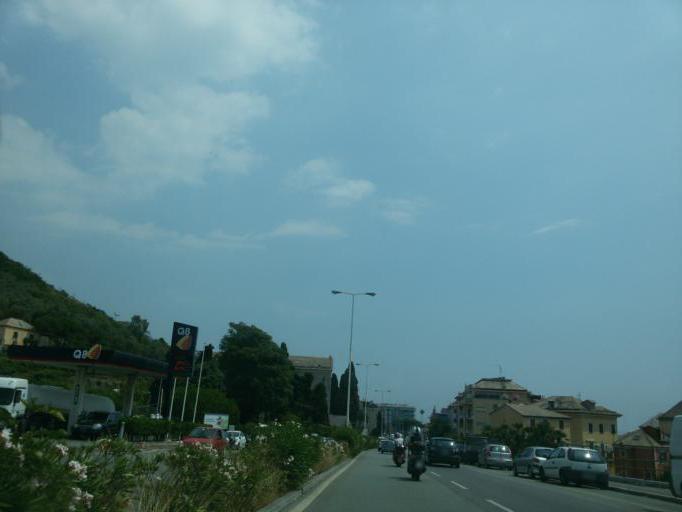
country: IT
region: Liguria
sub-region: Provincia di Genova
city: Bogliasco
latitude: 44.3889
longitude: 9.0144
